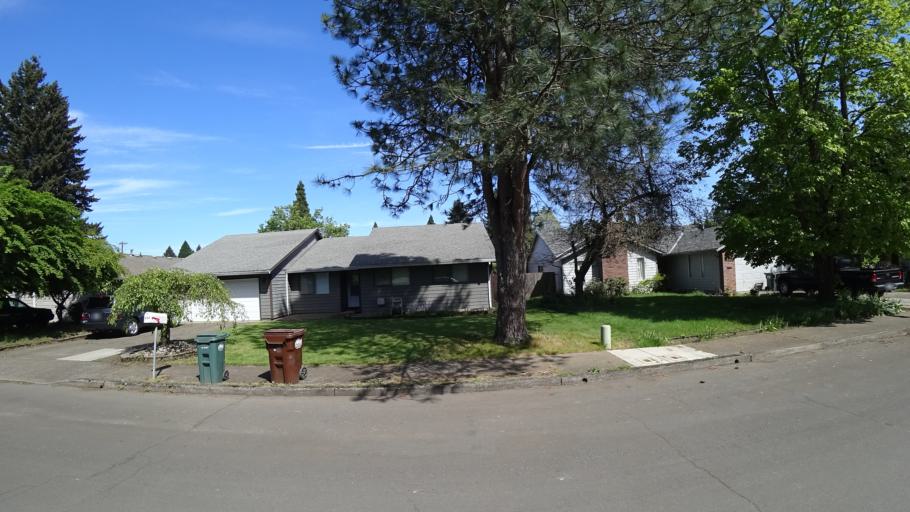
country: US
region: Oregon
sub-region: Washington County
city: Hillsboro
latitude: 45.5155
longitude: -122.9467
